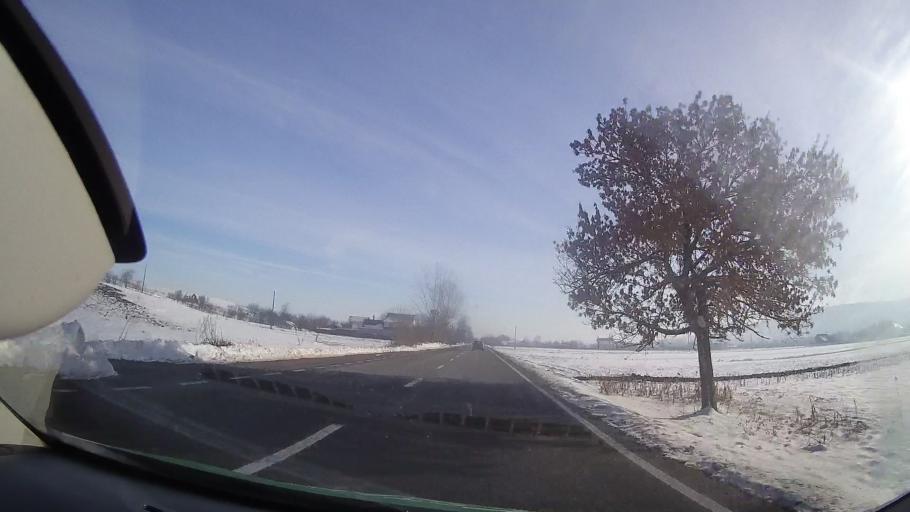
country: RO
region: Neamt
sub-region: Comuna Negresti
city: Negresti
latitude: 47.0642
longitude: 26.3774
